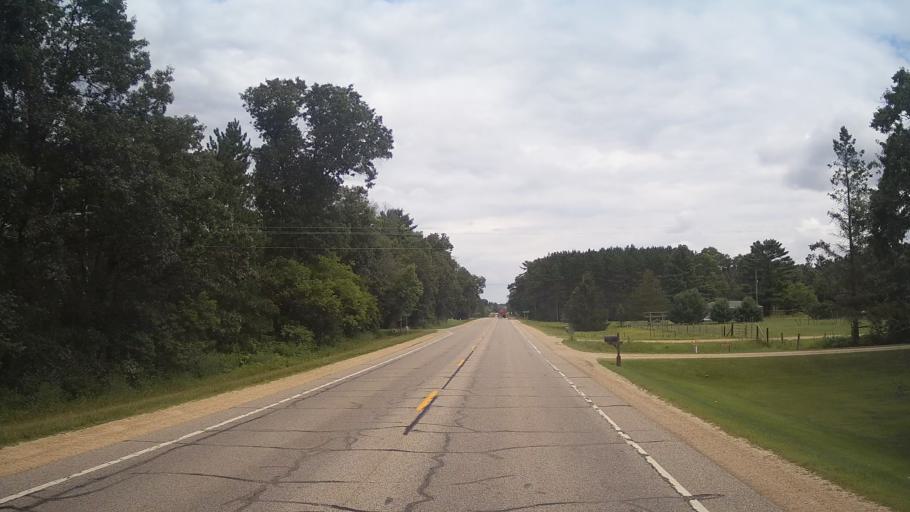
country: US
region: Wisconsin
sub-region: Waushara County
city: Wautoma
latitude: 44.0684
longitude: -89.3128
